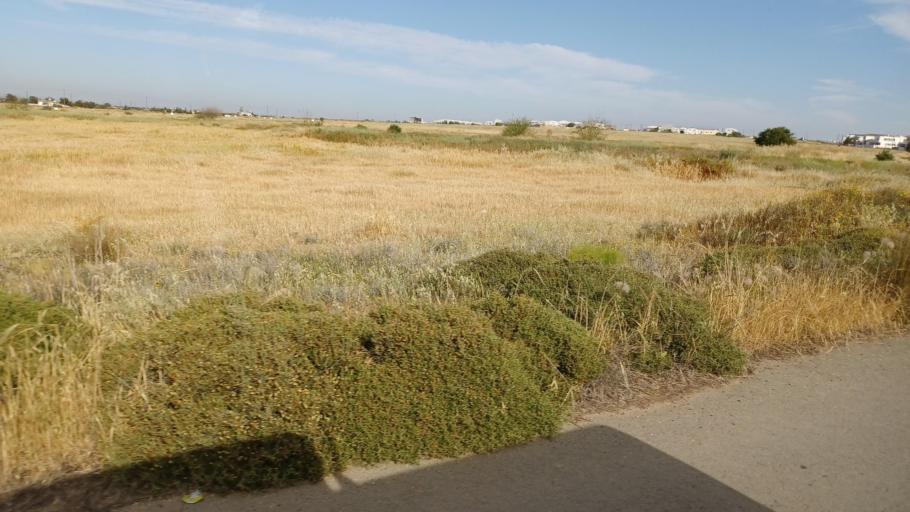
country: CY
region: Lefkosia
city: Kokkinotrimithia
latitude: 35.1633
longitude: 33.1994
